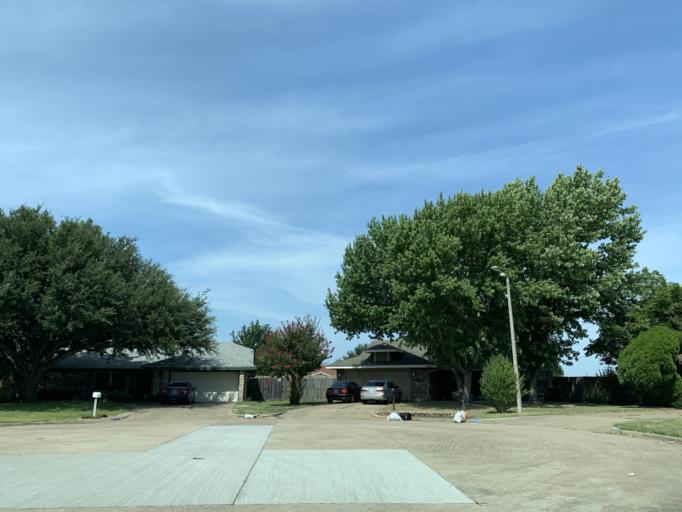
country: US
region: Texas
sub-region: Dallas County
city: Grand Prairie
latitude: 32.6701
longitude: -97.0435
